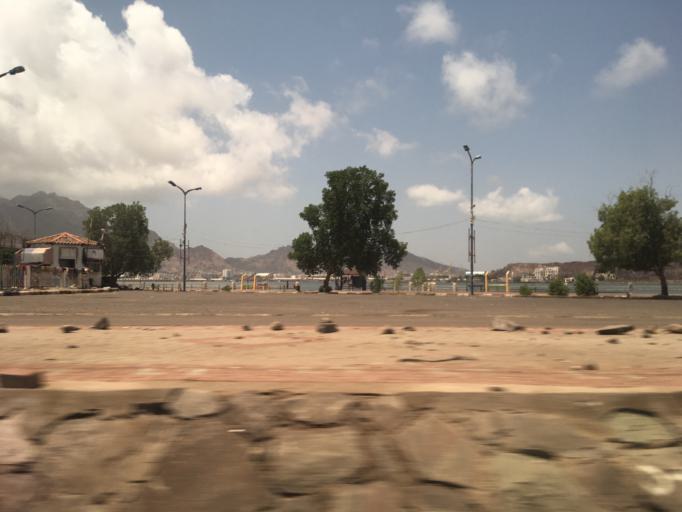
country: YE
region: Aden
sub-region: Khur Maksar
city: Khawr Maksar
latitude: 12.8069
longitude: 45.0268
